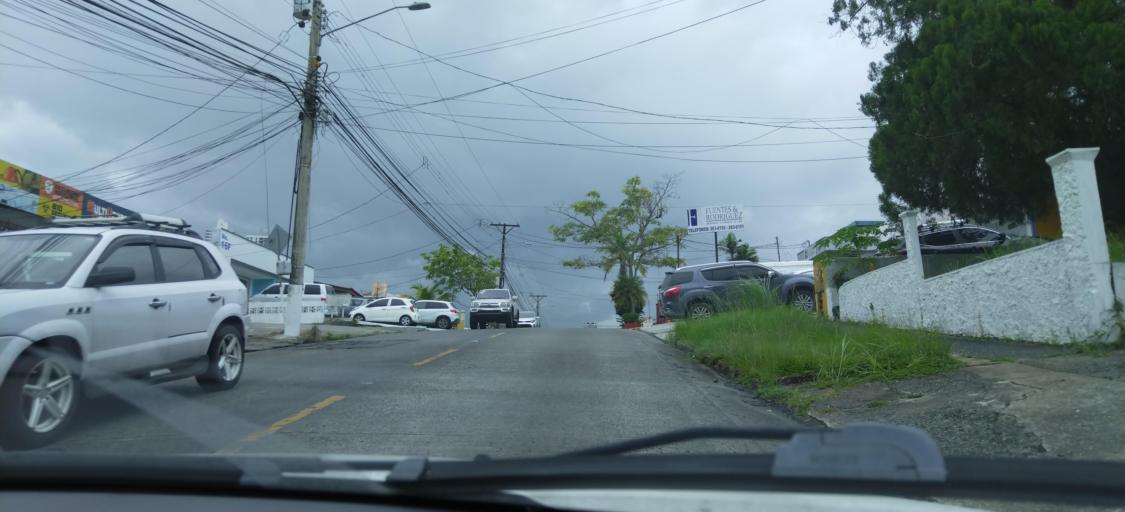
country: PA
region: Panama
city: Panama
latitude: 9.0108
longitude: -79.5404
